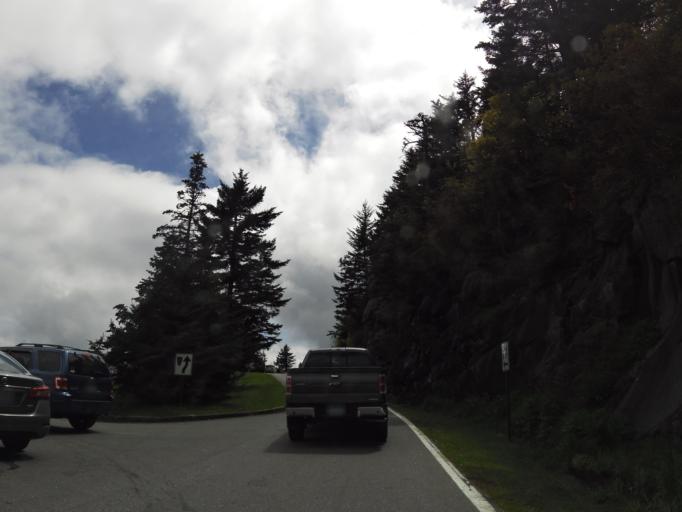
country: US
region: North Carolina
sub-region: Swain County
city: Bryson City
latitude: 35.5573
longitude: -83.4939
